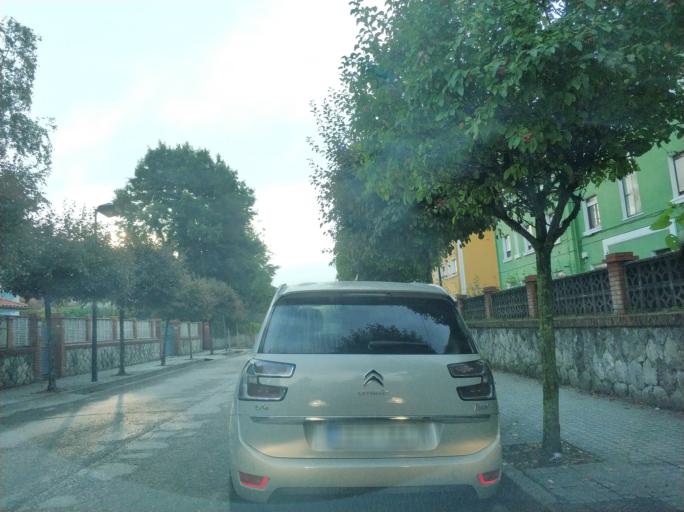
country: ES
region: Cantabria
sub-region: Provincia de Cantabria
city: Torrelavega
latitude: 43.3546
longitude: -4.0581
